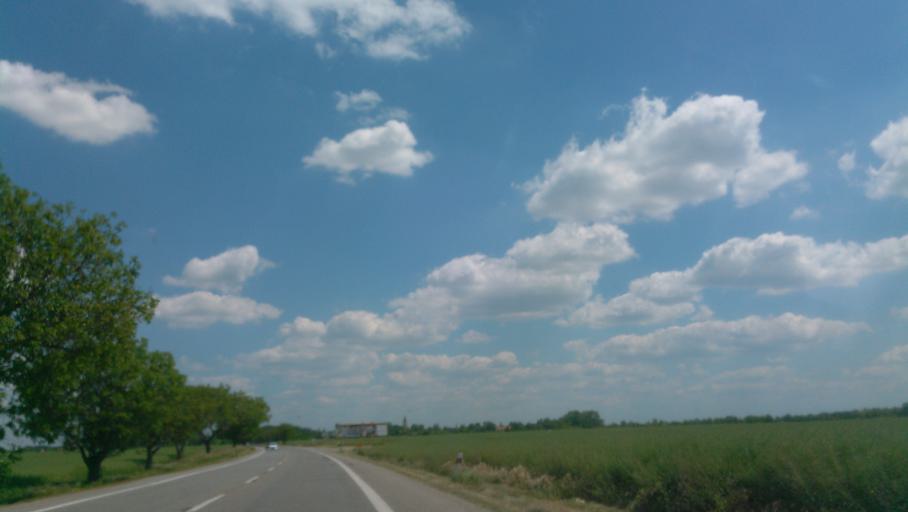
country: SK
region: Trnavsky
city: Samorin
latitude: 48.0105
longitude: 17.3533
